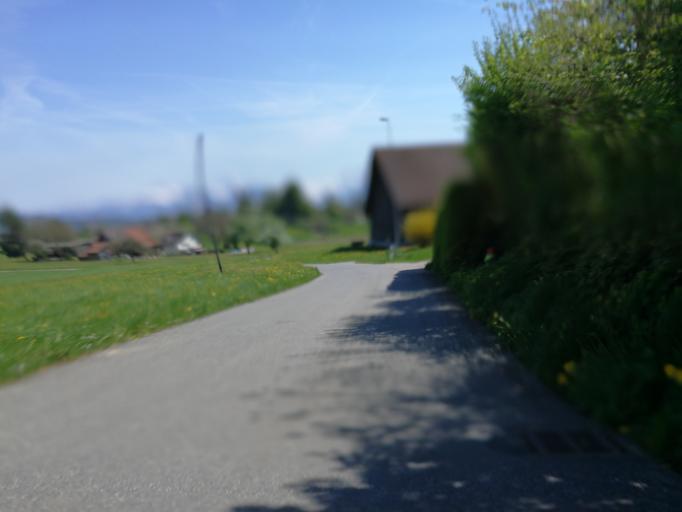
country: CH
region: Zurich
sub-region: Bezirk Hinwil
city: Bubikon
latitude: 47.2725
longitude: 8.8062
